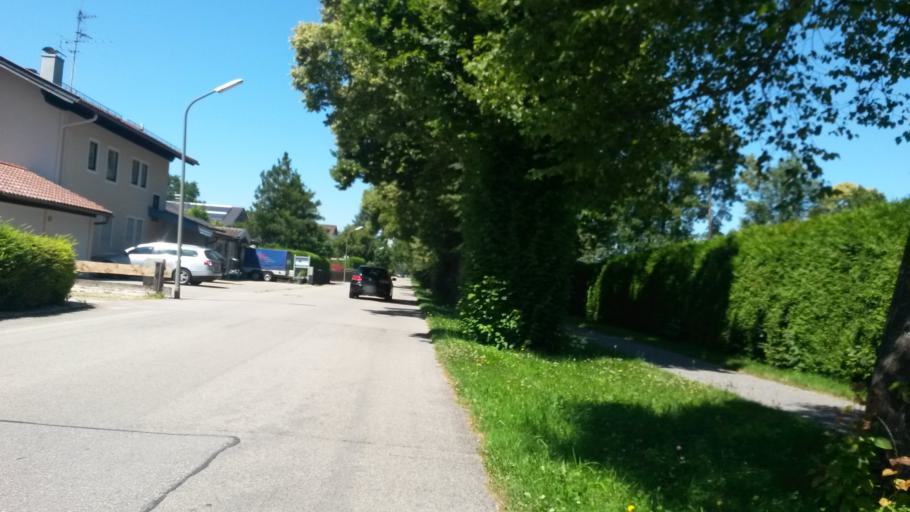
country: DE
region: Bavaria
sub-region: Upper Bavaria
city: Bernau am Chiemsee
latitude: 47.8213
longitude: 12.3901
